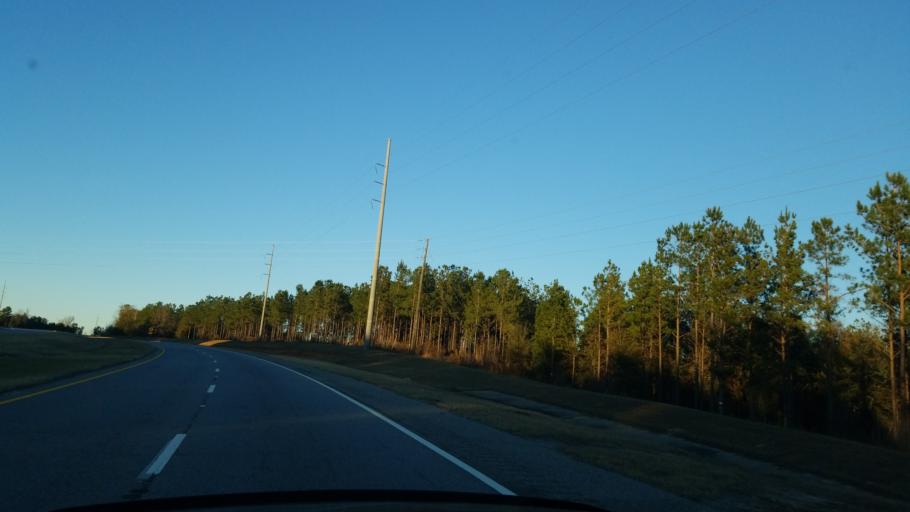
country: US
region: Georgia
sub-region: Chattahoochee County
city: Cusseta
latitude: 32.2755
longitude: -84.7810
